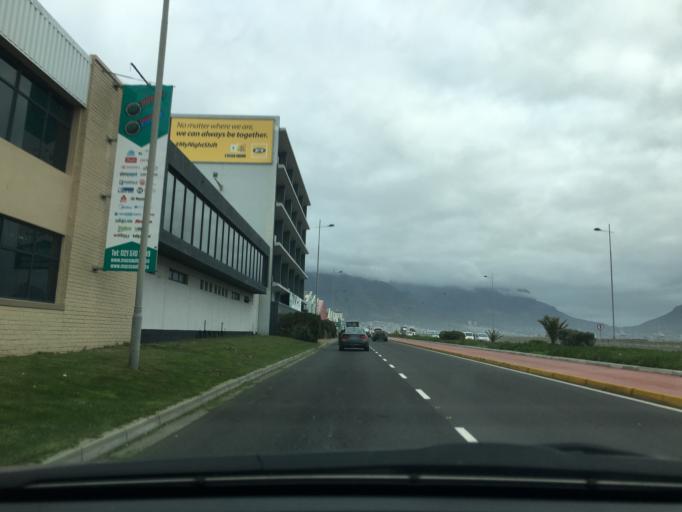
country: ZA
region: Western Cape
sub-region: City of Cape Town
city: Sunset Beach
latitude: -33.8974
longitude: 18.4808
